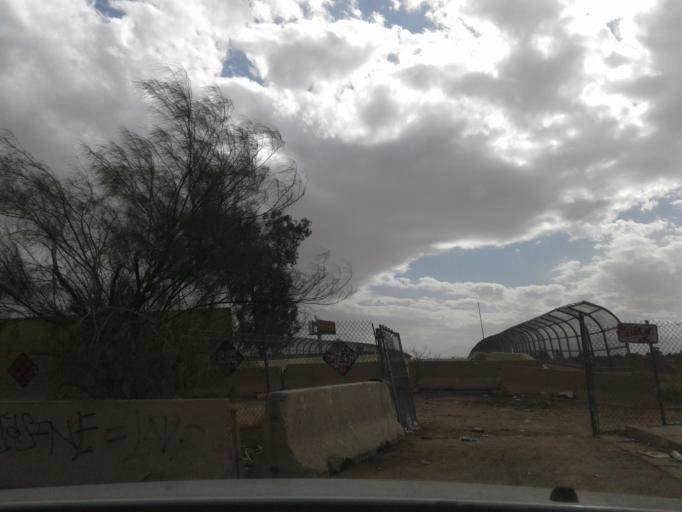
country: US
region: Arizona
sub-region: Maricopa County
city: Tolleson
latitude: 33.4639
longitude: -112.1952
